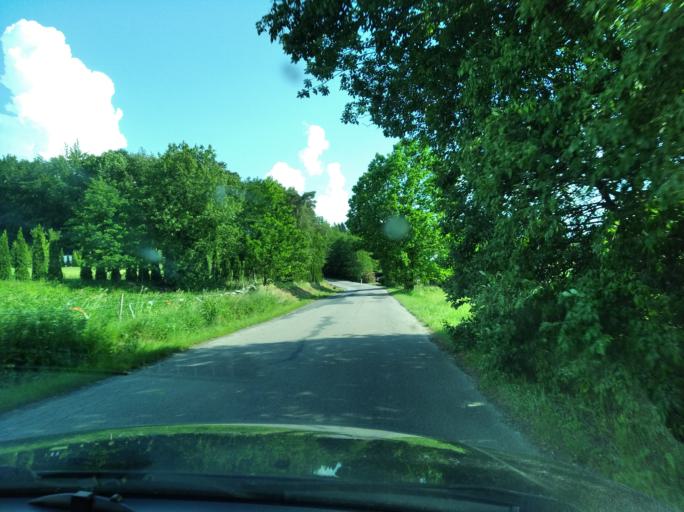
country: PL
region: Subcarpathian Voivodeship
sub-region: Powiat jaroslawski
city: Kramarzowka
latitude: 49.8599
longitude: 22.5159
